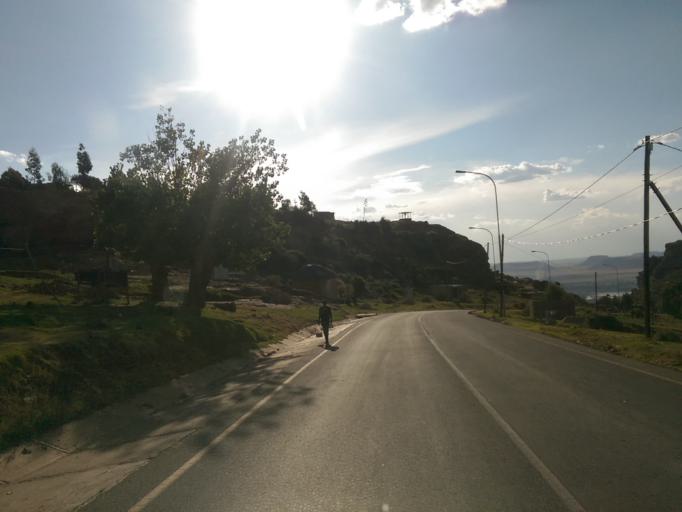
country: LS
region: Maseru
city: Maseru
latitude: -29.3173
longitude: 27.5556
